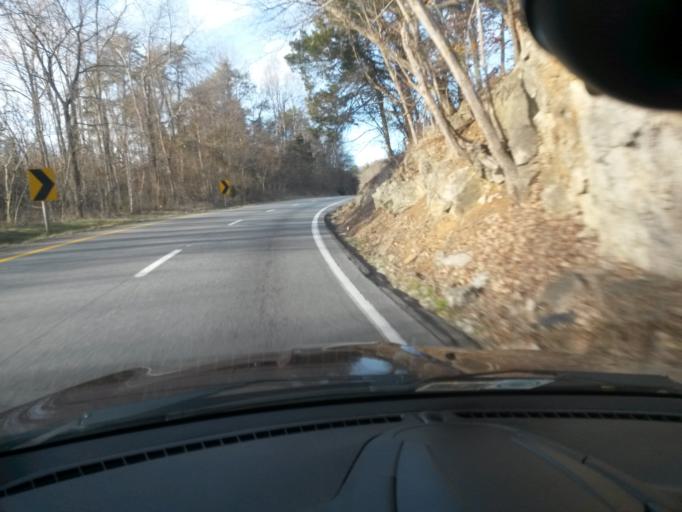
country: US
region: Virginia
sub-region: Botetourt County
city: Fincastle
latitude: 37.5947
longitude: -79.8357
